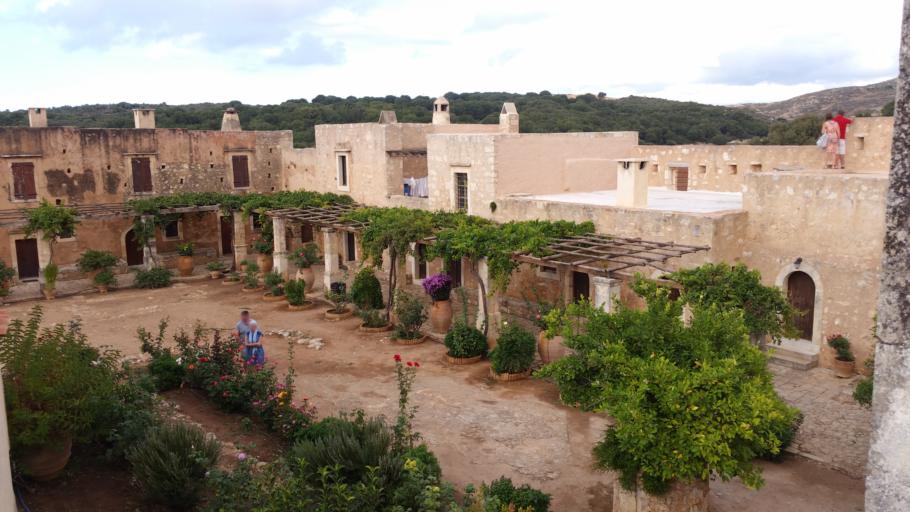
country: GR
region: Crete
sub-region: Nomos Rethymnis
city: Agia Foteini
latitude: 35.3097
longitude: 24.6295
